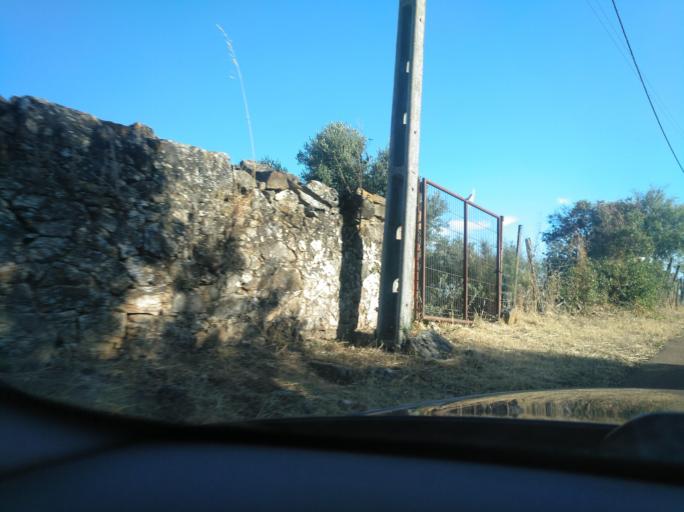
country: PT
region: Portalegre
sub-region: Elvas
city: Elvas
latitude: 38.8627
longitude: -7.1564
